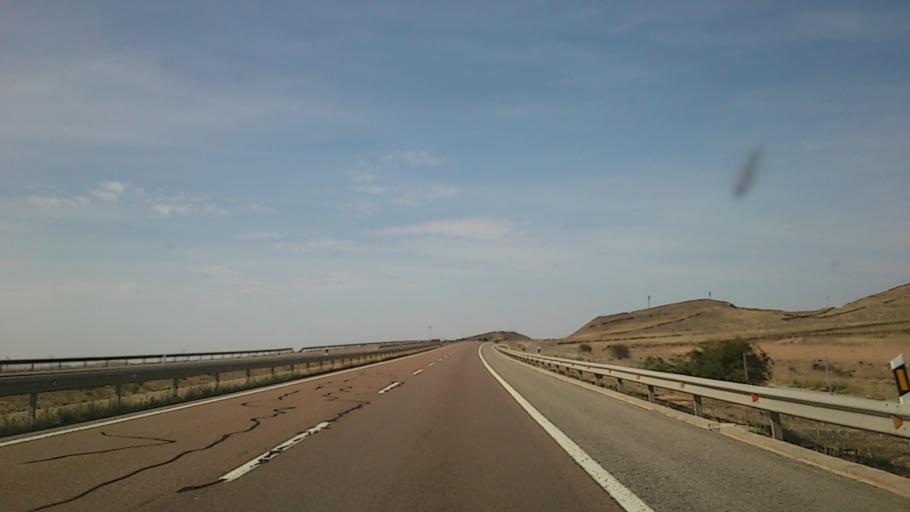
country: ES
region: Aragon
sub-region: Provincia de Teruel
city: Singra
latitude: 40.6485
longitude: -1.3169
